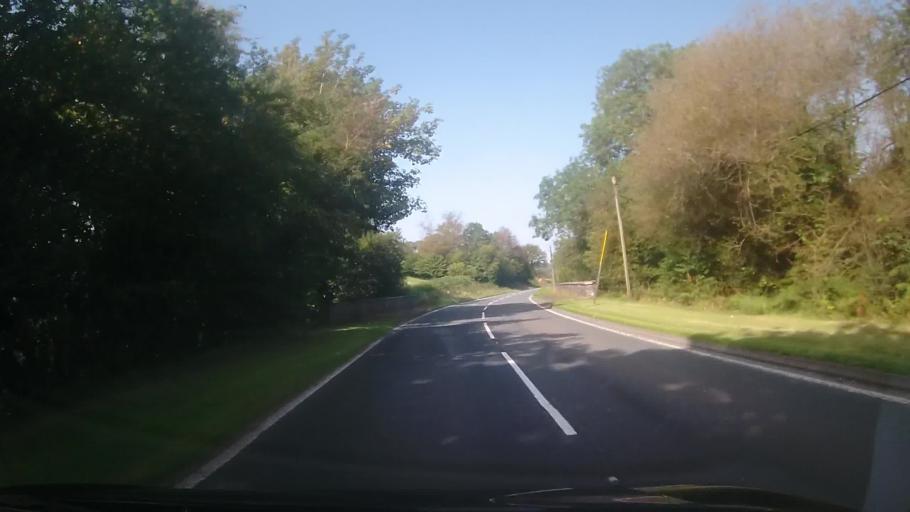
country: GB
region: Wales
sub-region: Sir Powys
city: Builth Wells
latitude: 52.1405
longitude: -3.5696
